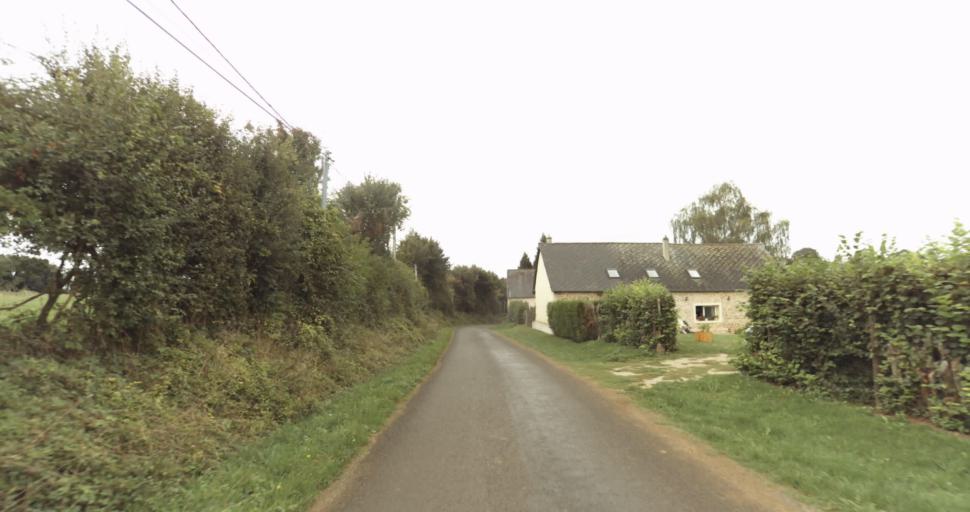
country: FR
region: Lower Normandy
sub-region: Departement de l'Orne
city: Sainte-Gauburge-Sainte-Colombe
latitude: 48.7321
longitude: 0.3785
